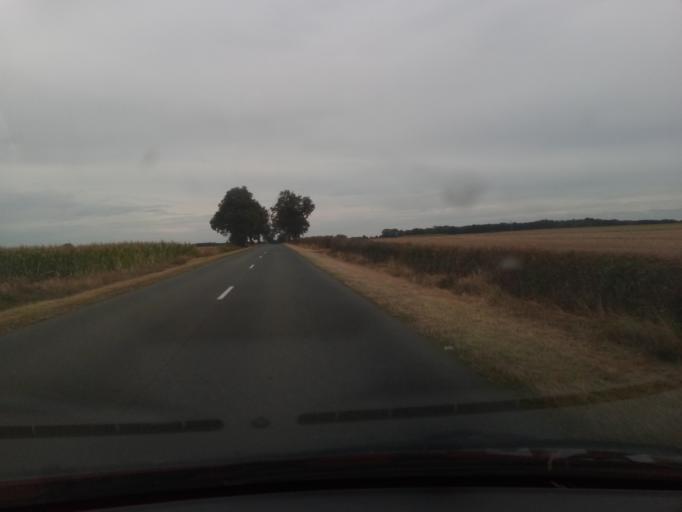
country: FR
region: Poitou-Charentes
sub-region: Departement de la Vienne
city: Montmorillon
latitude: 46.4995
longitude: 0.7795
